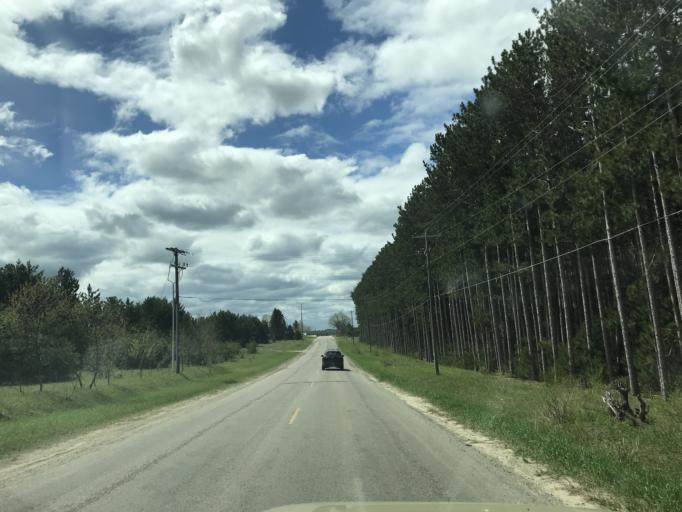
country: US
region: Michigan
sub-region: Otsego County
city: Gaylord
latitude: 45.0372
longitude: -84.6942
